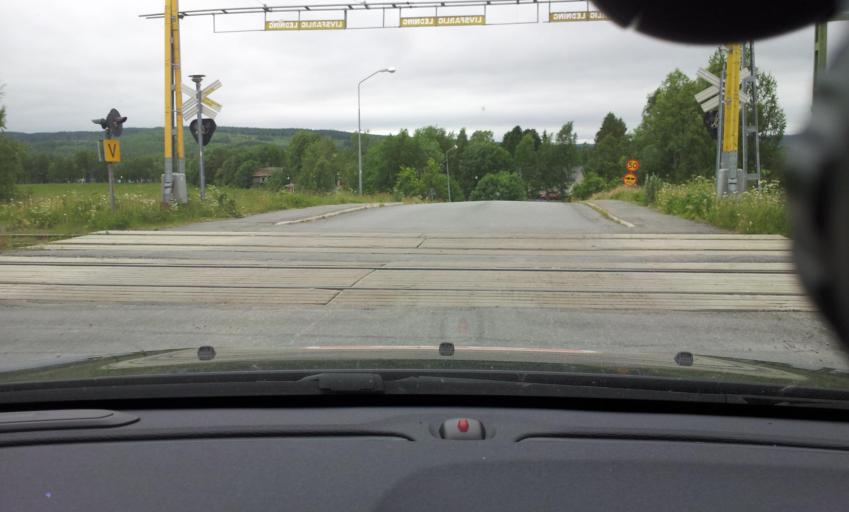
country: SE
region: Jaemtland
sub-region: Are Kommun
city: Jarpen
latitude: 63.3080
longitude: 13.6631
